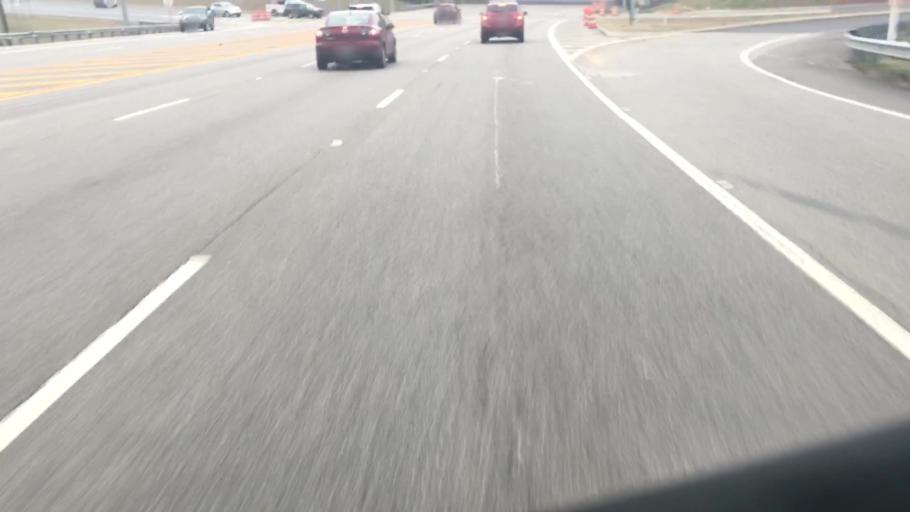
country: US
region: Alabama
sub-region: Shelby County
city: Helena
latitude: 33.3574
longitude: -86.8535
